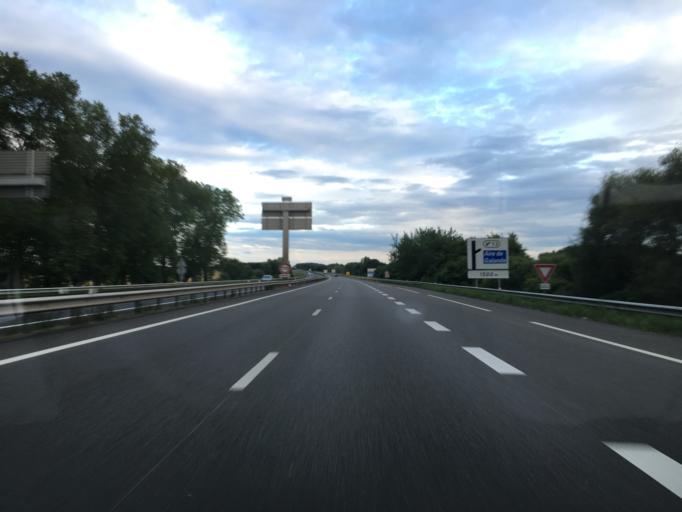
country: FR
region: Ile-de-France
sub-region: Departement de Seine-et-Marne
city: Moissy-Cramayel
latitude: 48.6288
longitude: 2.6288
